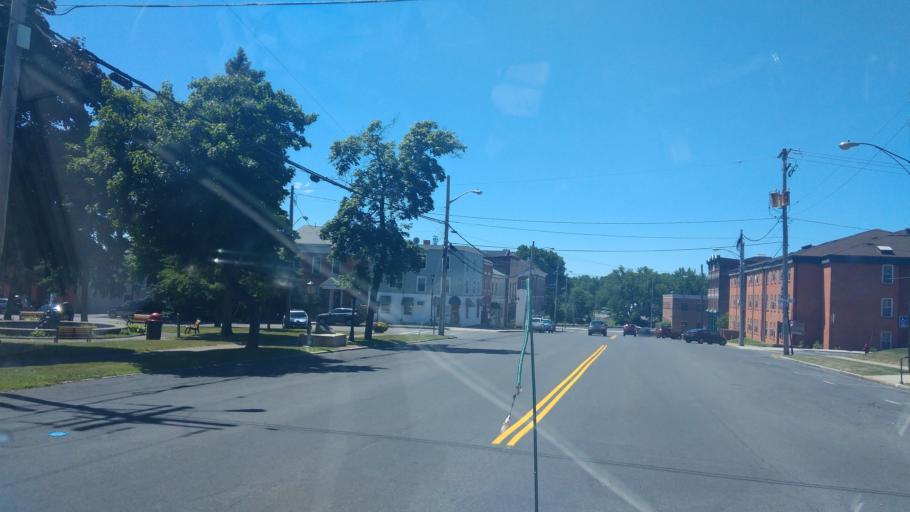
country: US
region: New York
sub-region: Wayne County
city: Lyons
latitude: 43.0639
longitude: -76.9941
